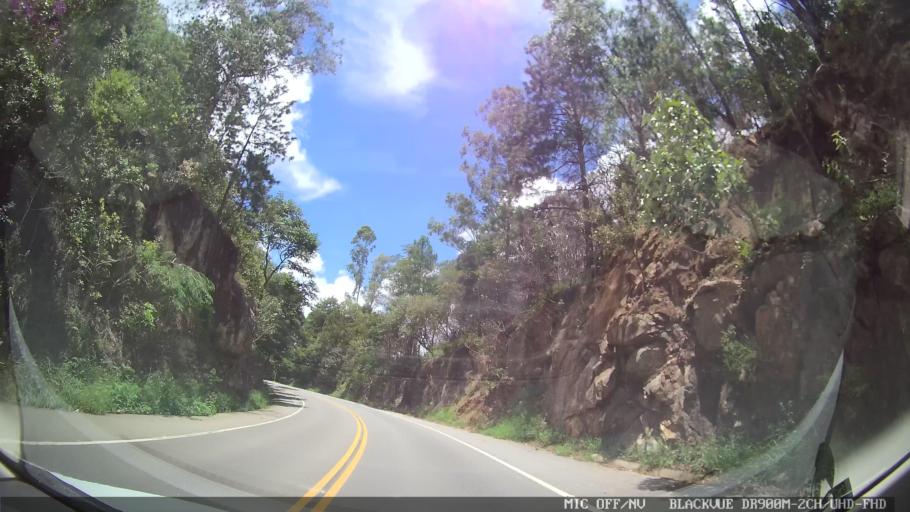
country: BR
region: Sao Paulo
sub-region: Amparo
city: Amparo
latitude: -22.7769
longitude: -46.7355
